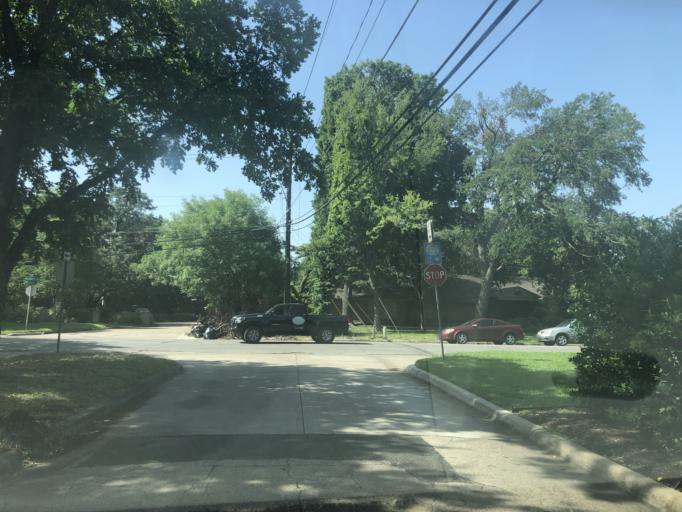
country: US
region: Texas
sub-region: Dallas County
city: University Park
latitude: 32.8869
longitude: -96.8126
